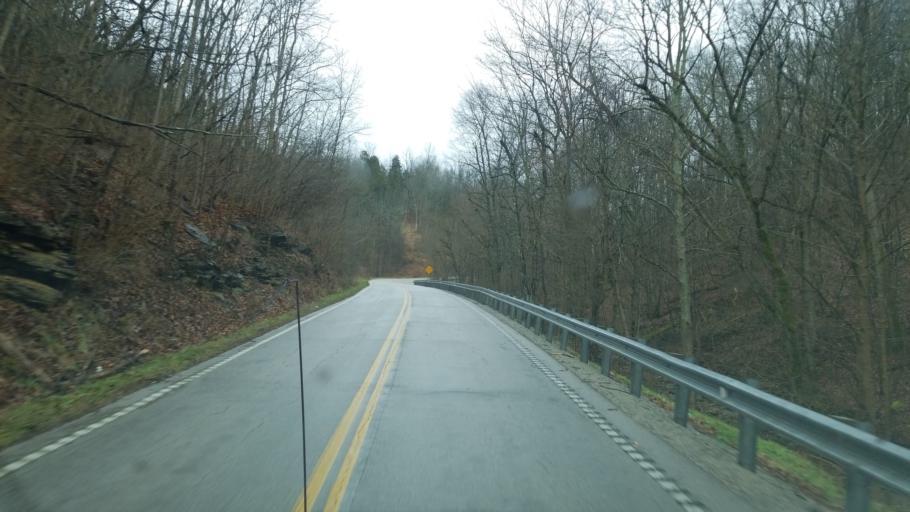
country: US
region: Kentucky
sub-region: Mason County
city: Maysville
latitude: 38.6110
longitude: -83.6903
